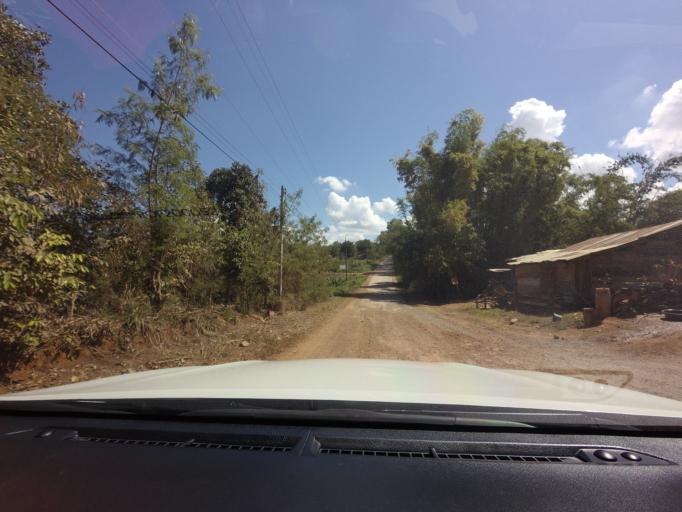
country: TH
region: Nakhon Ratchasima
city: Wang Nam Khiao
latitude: 14.4370
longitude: 101.7029
